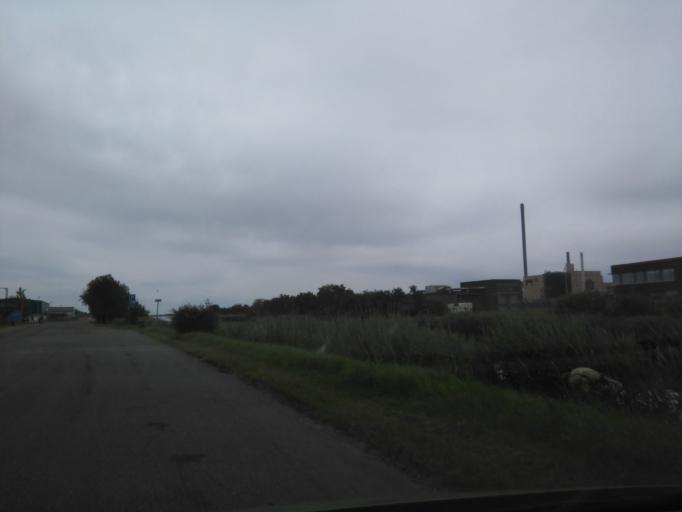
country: DK
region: Central Jutland
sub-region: Horsens Kommune
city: Horsens
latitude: 55.8561
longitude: 9.8543
